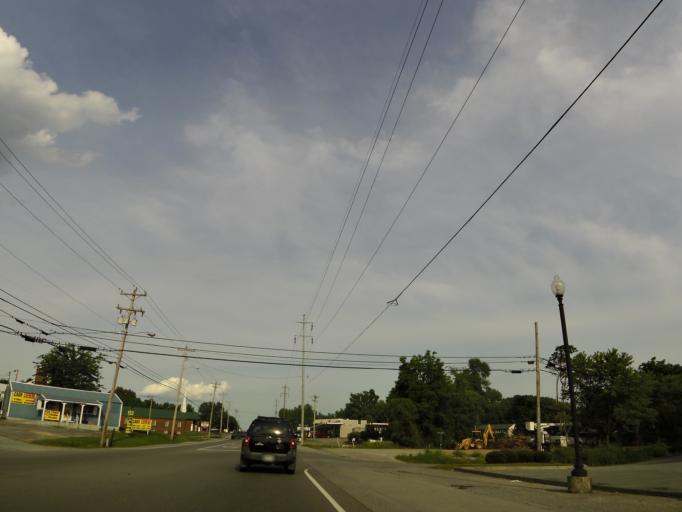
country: US
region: Tennessee
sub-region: Humphreys County
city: McEwen
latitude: 36.1075
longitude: -87.6338
